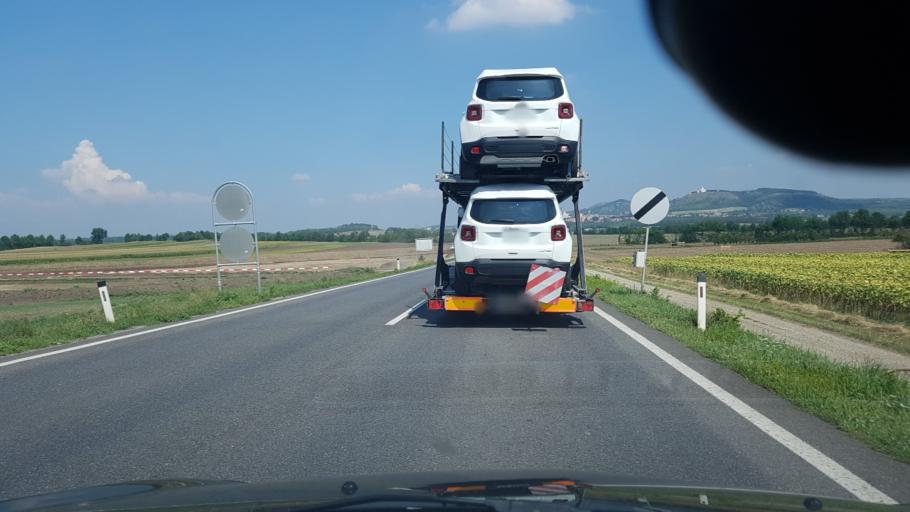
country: AT
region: Lower Austria
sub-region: Politischer Bezirk Mistelbach
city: Drasenhofen
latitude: 48.7710
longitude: 16.6430
